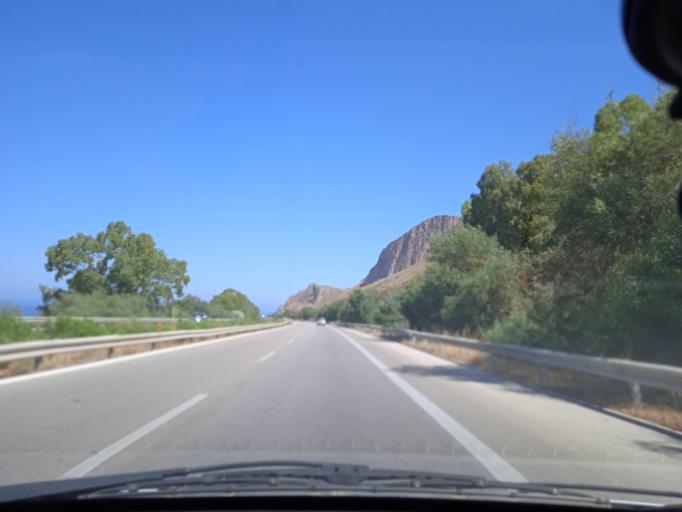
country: IT
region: Sicily
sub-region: Palermo
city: Agliandroni-Paternella
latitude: 38.1112
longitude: 13.0887
